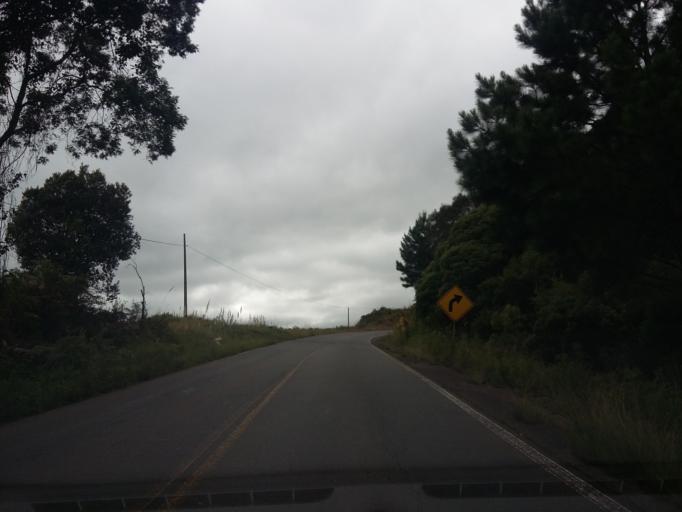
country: BR
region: Santa Catarina
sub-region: Lages
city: Lages
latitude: -27.8676
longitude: -50.1847
